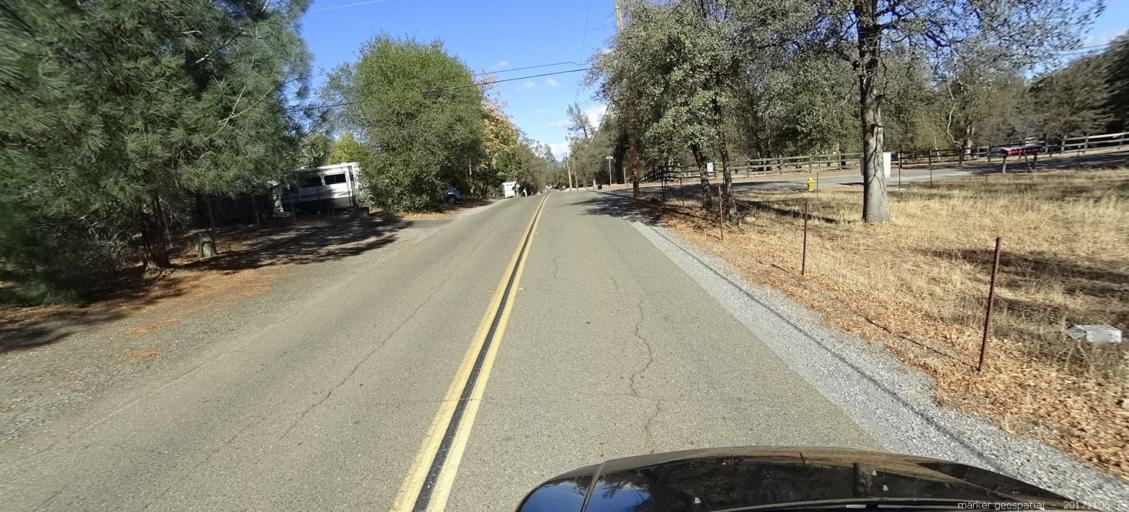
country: US
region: California
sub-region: Shasta County
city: Bella Vista
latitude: 40.6123
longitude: -122.2776
